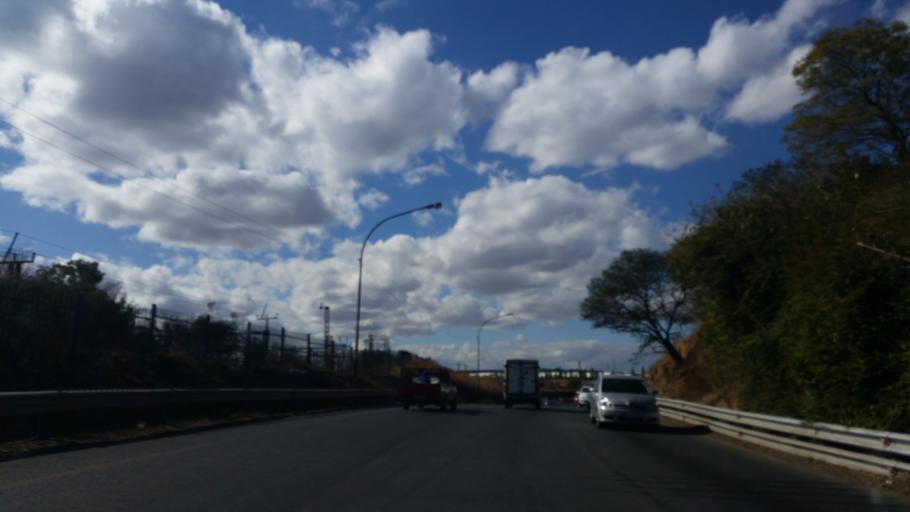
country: ZA
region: KwaZulu-Natal
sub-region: uThukela District Municipality
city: Ladysmith
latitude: -28.5498
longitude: 29.7913
